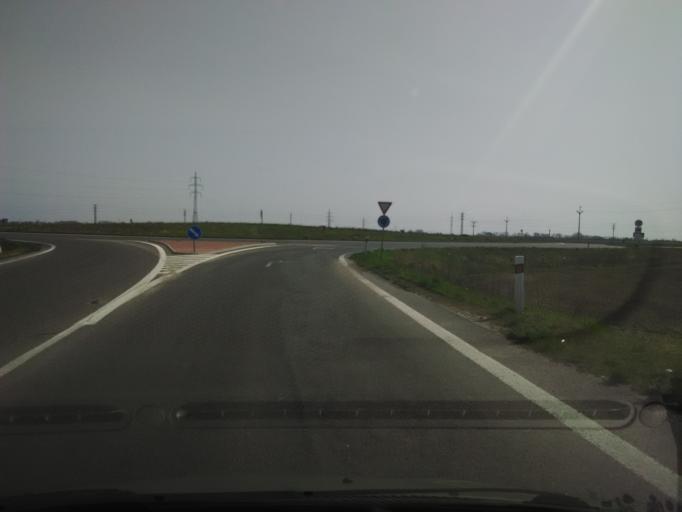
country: SK
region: Trnavsky
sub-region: Okres Galanta
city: Galanta
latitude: 48.1918
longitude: 17.7491
